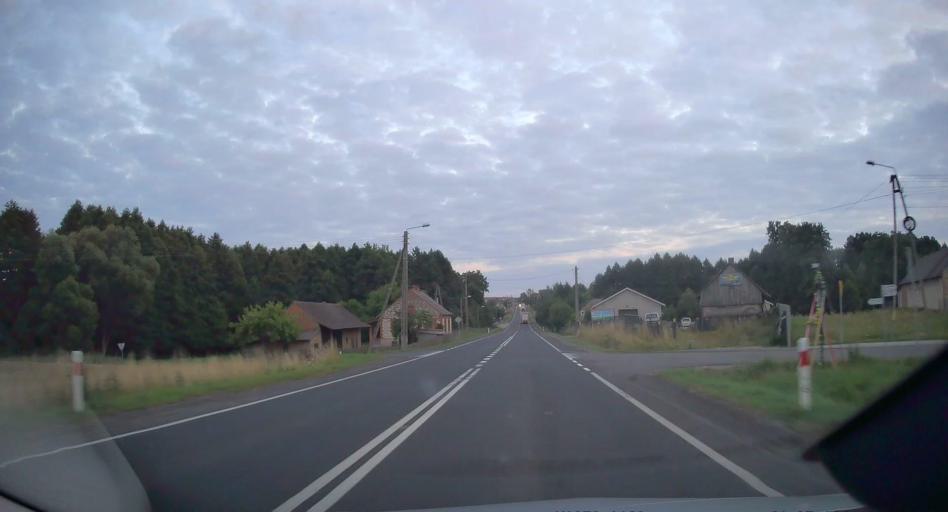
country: PL
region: Lodz Voivodeship
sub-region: Powiat wielunski
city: Patnow
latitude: 51.1216
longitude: 18.6099
